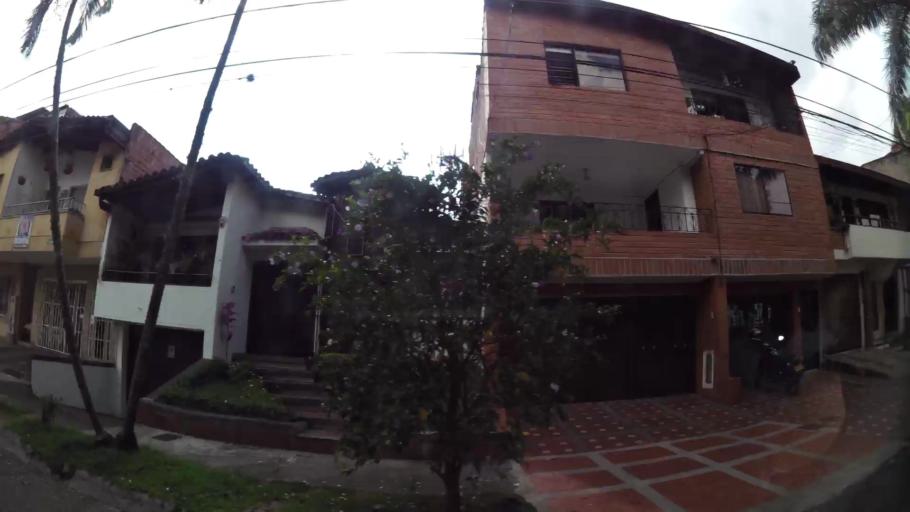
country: CO
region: Antioquia
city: Medellin
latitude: 6.2339
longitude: -75.5944
